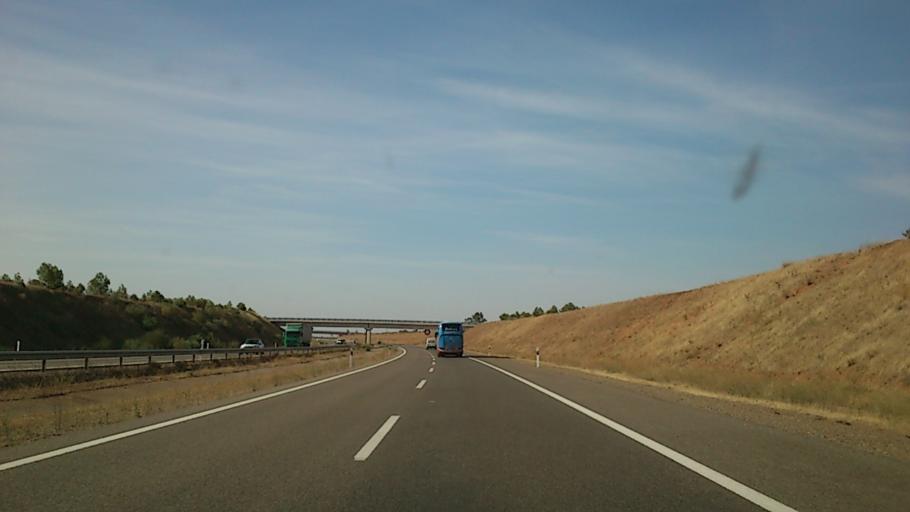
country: ES
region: Aragon
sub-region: Provincia de Zaragoza
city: Carinena
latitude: 41.3324
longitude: -1.2033
